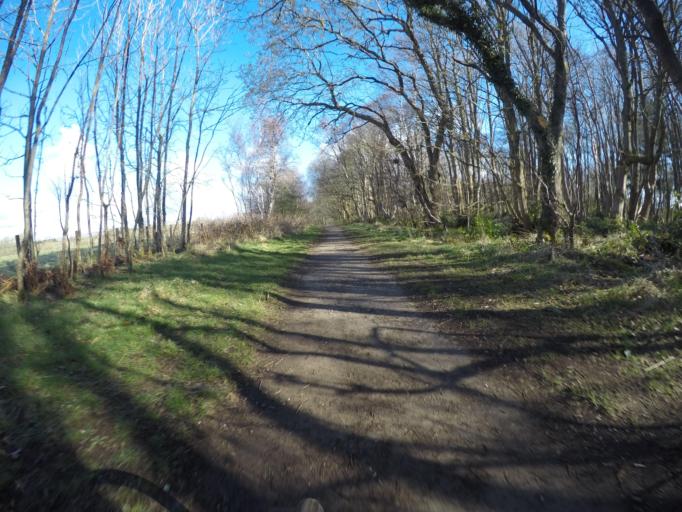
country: GB
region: Scotland
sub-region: North Ayrshire
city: Irvine
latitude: 55.6413
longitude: -4.6581
